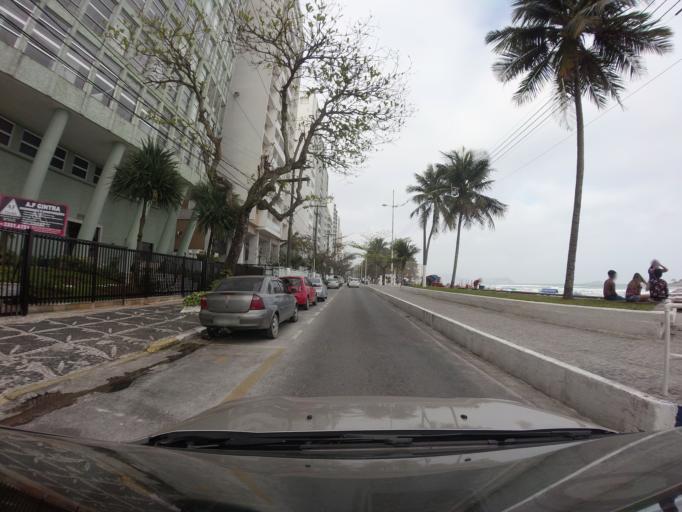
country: BR
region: Sao Paulo
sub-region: Guaruja
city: Guaruja
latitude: -23.9989
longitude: -46.2604
